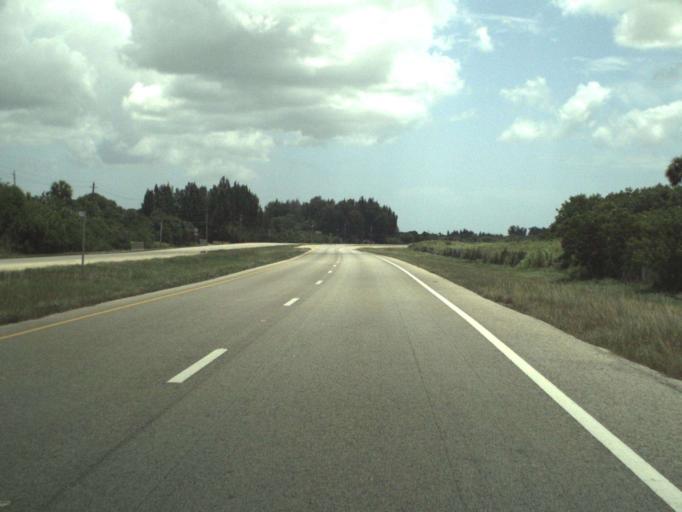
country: US
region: Florida
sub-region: Saint Lucie County
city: Fort Pierce South
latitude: 27.4095
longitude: -80.4194
